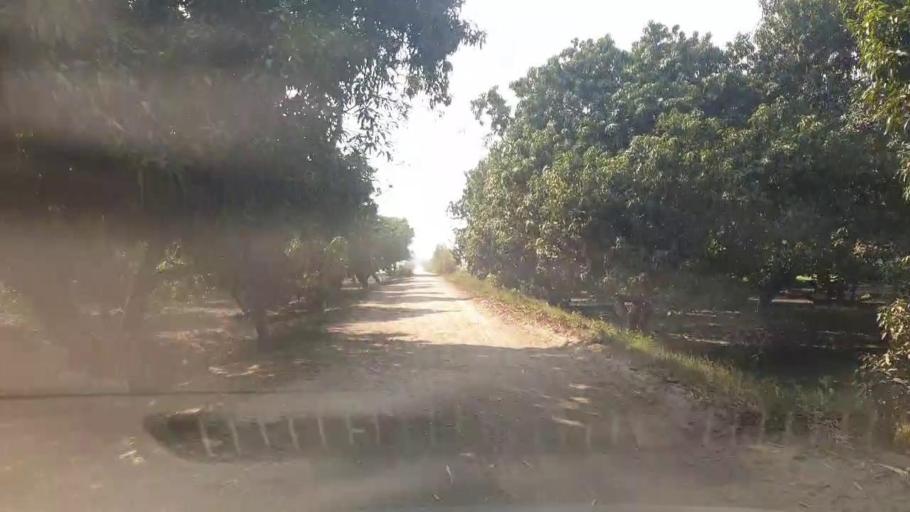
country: PK
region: Sindh
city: Tando Allahyar
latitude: 25.4642
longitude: 68.7820
